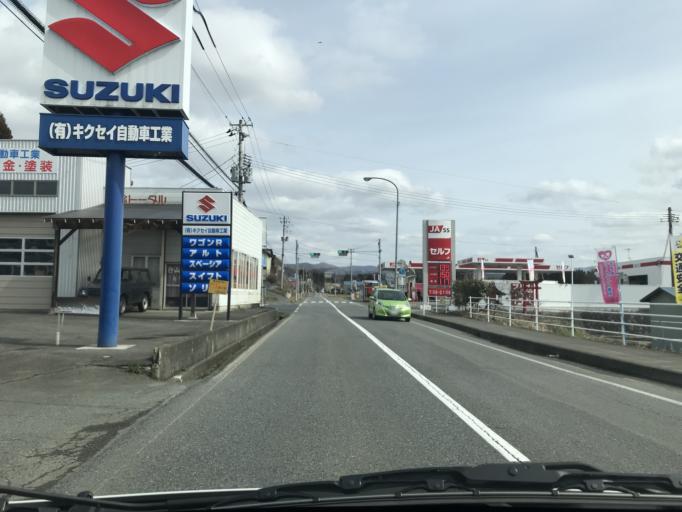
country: JP
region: Iwate
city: Kitakami
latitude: 39.2255
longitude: 141.2364
